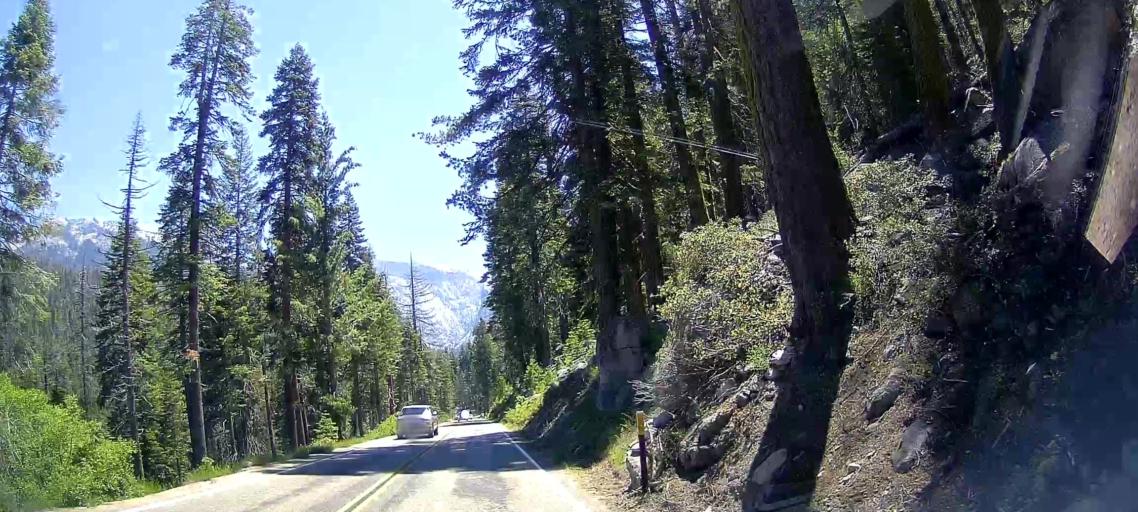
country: US
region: California
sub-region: Tulare County
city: Three Rivers
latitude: 36.6020
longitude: -118.7410
